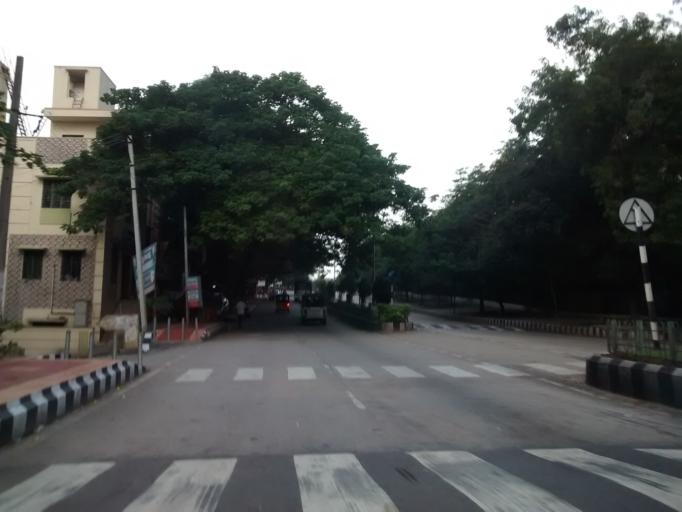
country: IN
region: Andhra Pradesh
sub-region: Chittoor
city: Akkarampalle
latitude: 13.6502
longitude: 79.4138
